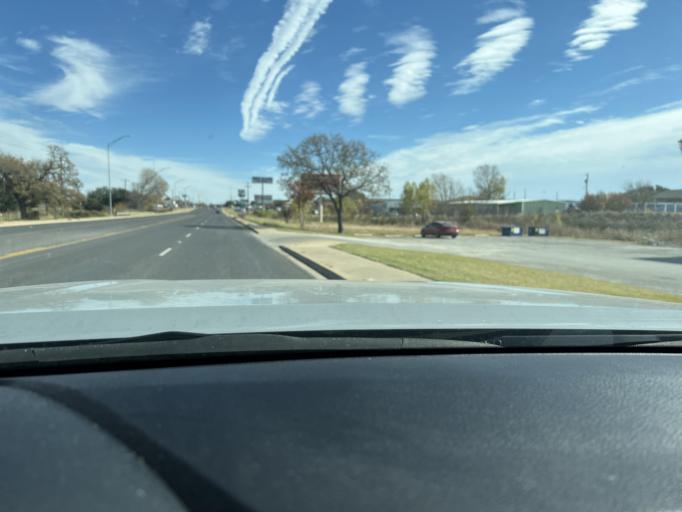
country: US
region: Texas
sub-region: Eastland County
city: Eastland
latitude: 32.4017
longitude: -98.8035
